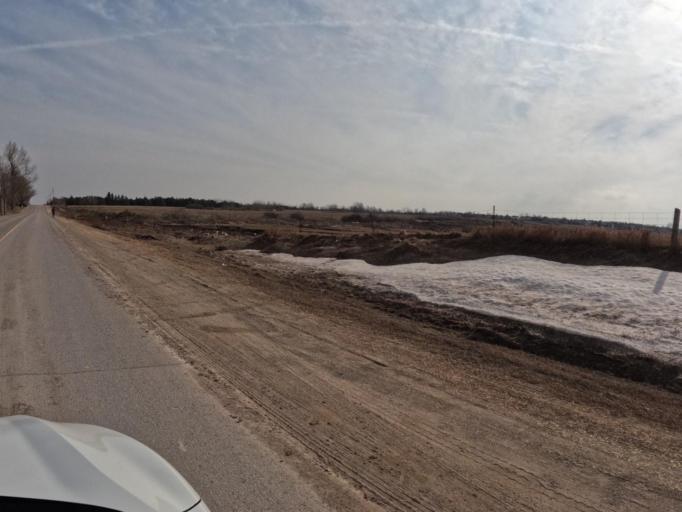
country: CA
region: Ontario
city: Orangeville
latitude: 43.8943
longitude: -80.2664
